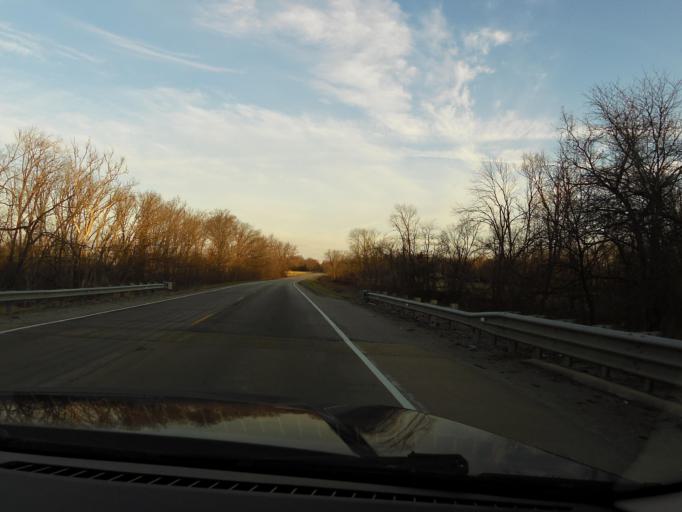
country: US
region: Illinois
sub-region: Fayette County
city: Vandalia
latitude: 38.8183
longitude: -89.0873
